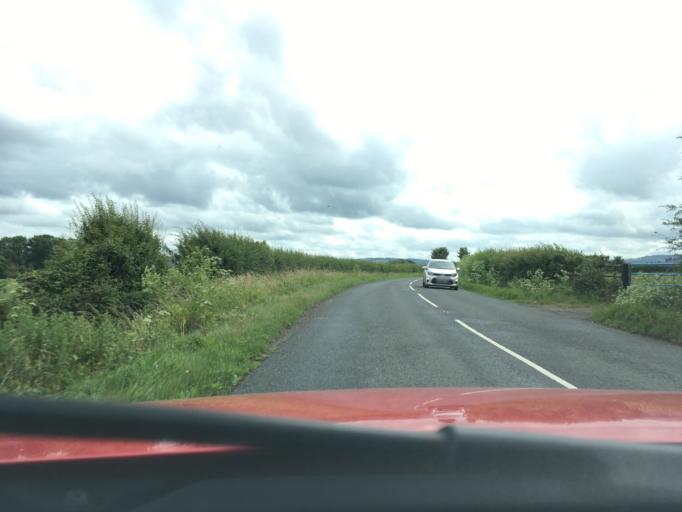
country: GB
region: England
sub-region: Worcestershire
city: Evesham
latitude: 52.0380
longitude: -1.9628
